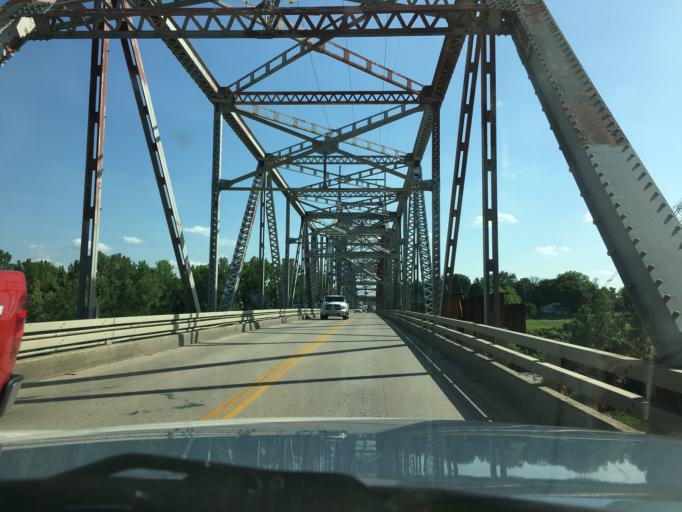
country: US
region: Missouri
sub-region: Franklin County
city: Washington
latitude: 38.5572
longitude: -90.9985
